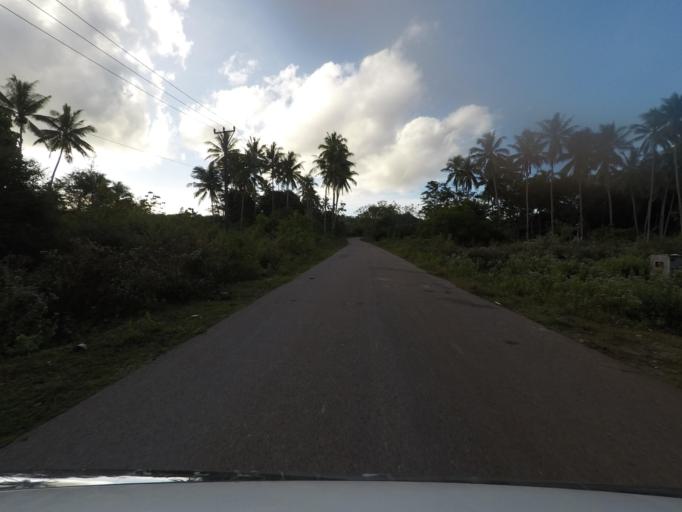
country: TL
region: Lautem
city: Lospalos
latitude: -8.4300
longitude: 127.0036
